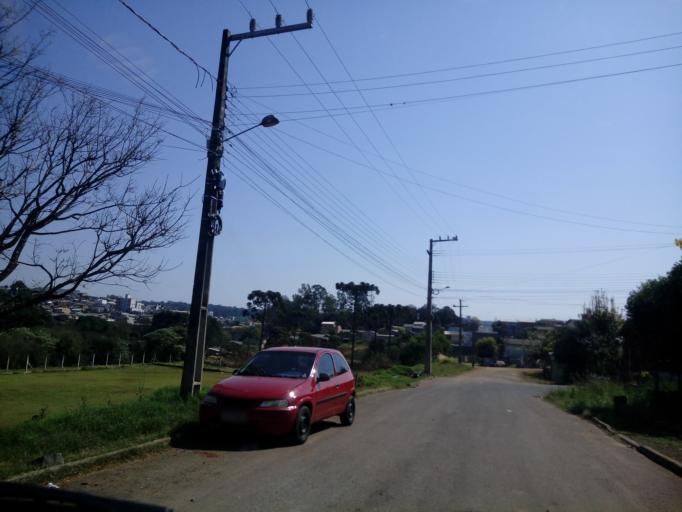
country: BR
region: Santa Catarina
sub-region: Chapeco
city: Chapeco
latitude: -27.1068
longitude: -52.6836
